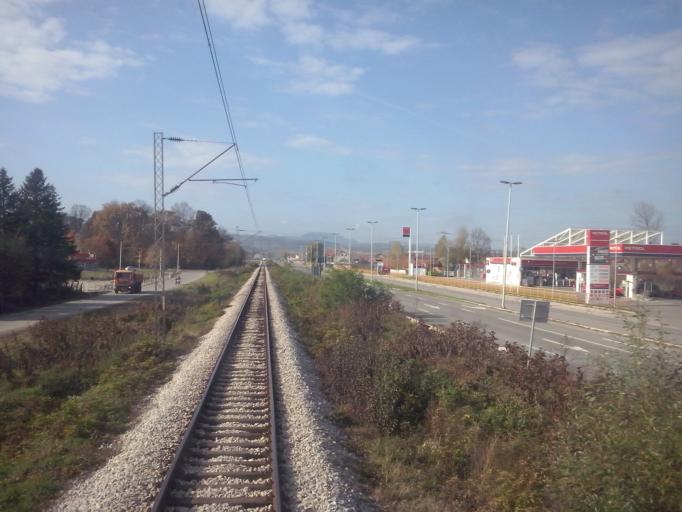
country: RS
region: Central Serbia
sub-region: Kolubarski Okrug
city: Valjevo
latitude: 44.2845
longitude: 19.9383
